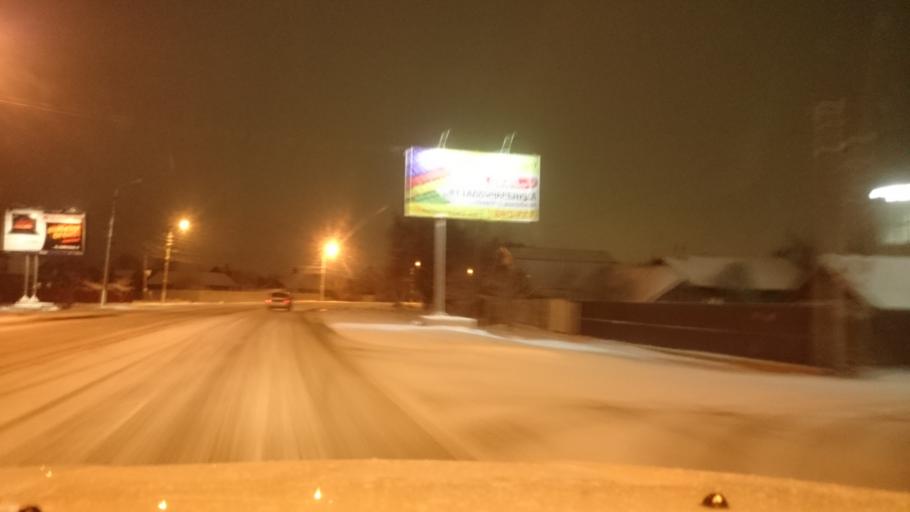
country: RU
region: Tula
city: Mendeleyevskiy
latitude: 54.1942
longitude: 37.5453
